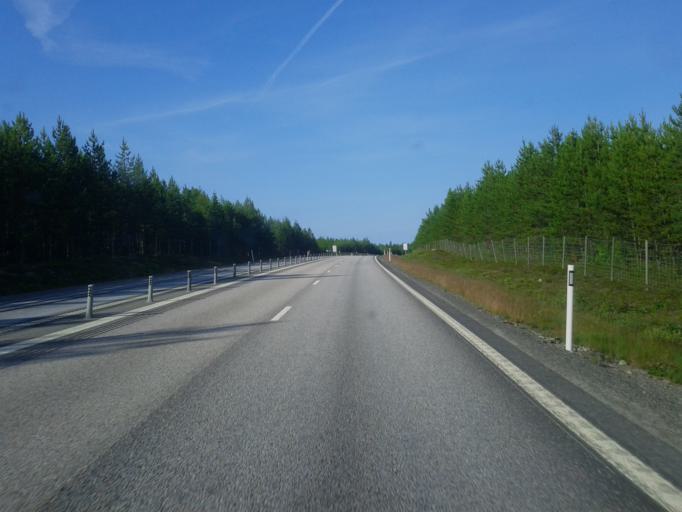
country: SE
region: Vaesterbotten
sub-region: Umea Kommun
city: Saevar
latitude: 63.9838
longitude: 20.7330
